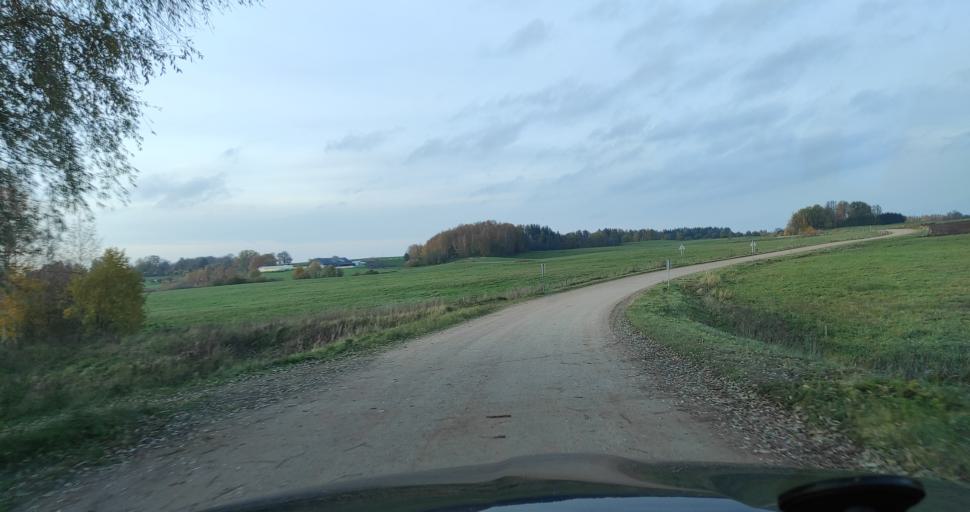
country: LV
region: Aizpute
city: Aizpute
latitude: 56.6482
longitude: 21.7954
